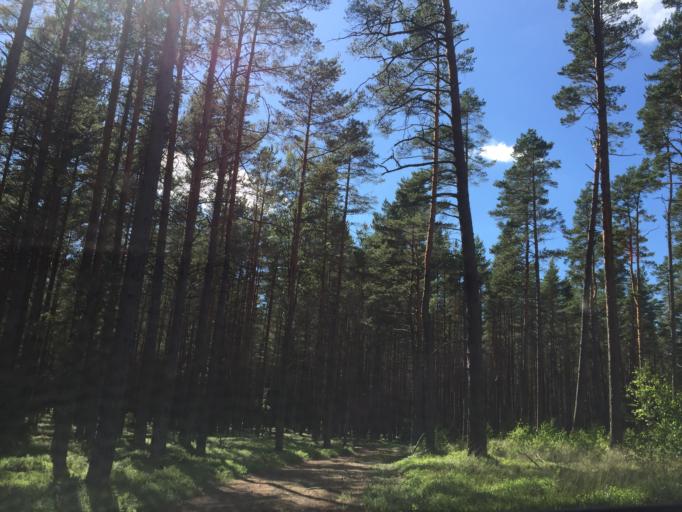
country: LV
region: Ventspils
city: Ventspils
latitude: 57.4731
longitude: 21.6507
